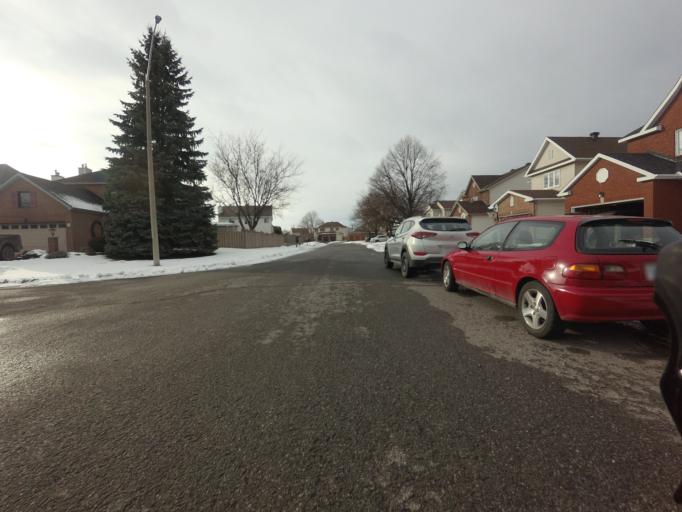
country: CA
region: Ontario
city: Bells Corners
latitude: 45.2665
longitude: -75.7690
